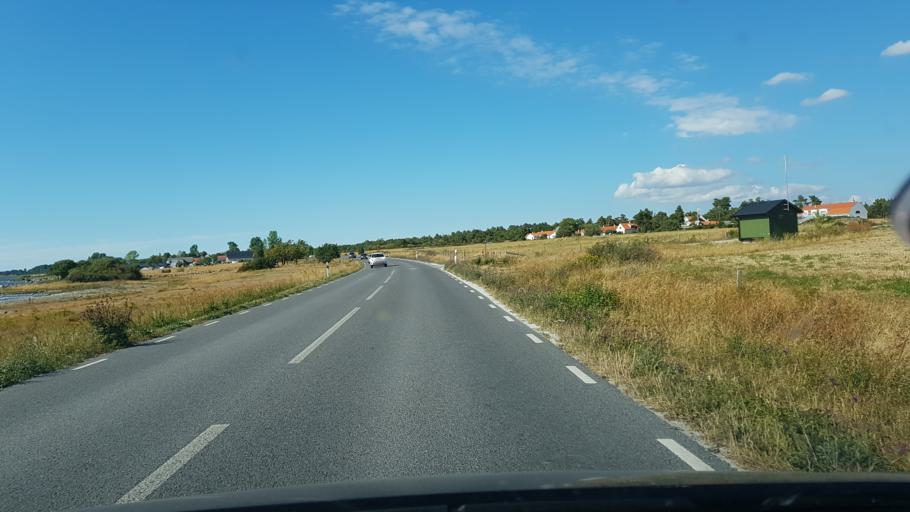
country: SE
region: Gotland
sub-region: Gotland
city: Klintehamn
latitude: 57.4256
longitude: 18.1495
